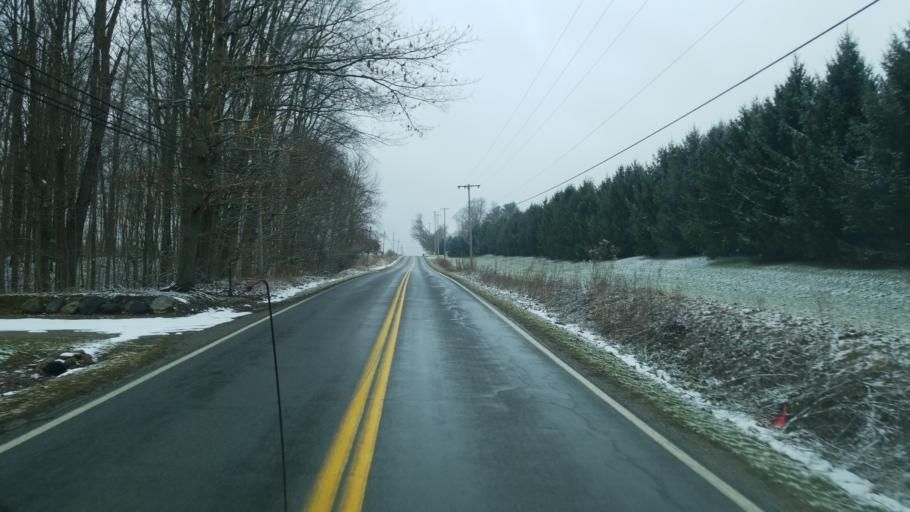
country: US
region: Ohio
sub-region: Portage County
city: Mantua
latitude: 41.2840
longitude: -81.2574
